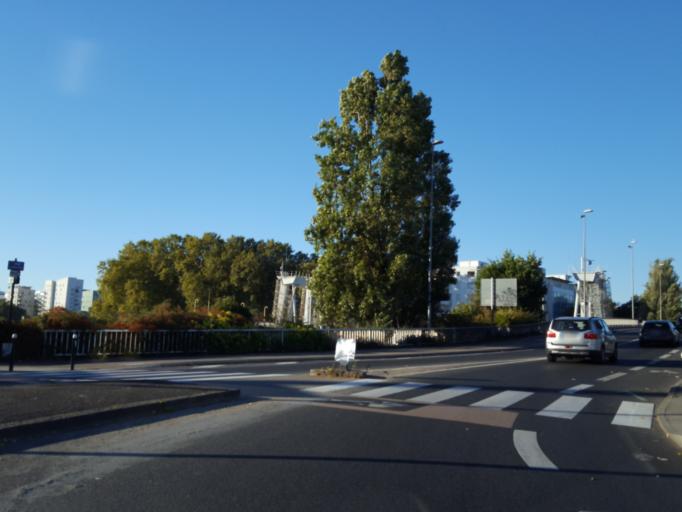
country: FR
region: Pays de la Loire
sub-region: Departement de la Loire-Atlantique
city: Nantes
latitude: 47.2136
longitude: -1.5398
